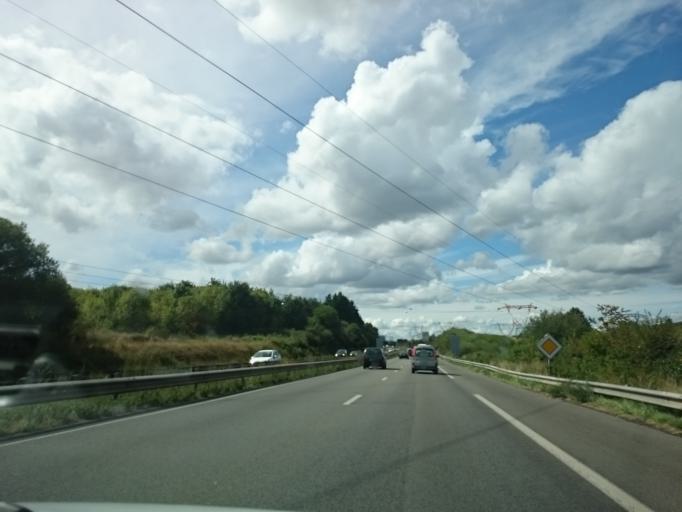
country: FR
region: Pays de la Loire
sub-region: Departement de la Loire-Atlantique
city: Bouguenais
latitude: 47.1751
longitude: -1.5958
